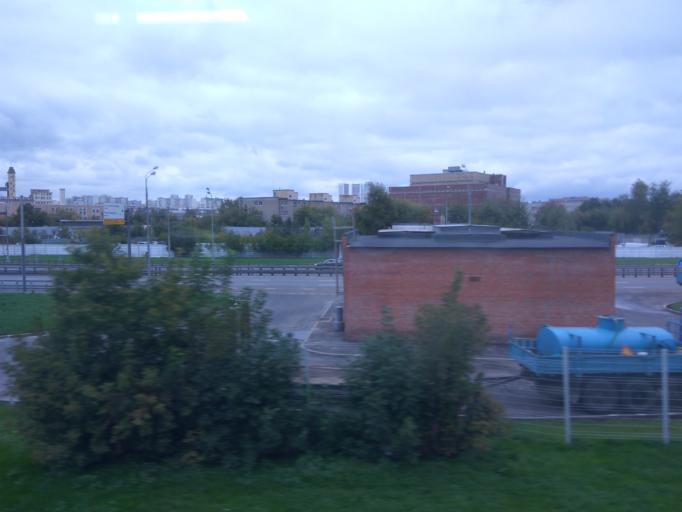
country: RU
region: Moskovskaya
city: Presnenskiy
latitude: 55.7650
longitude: 37.5187
